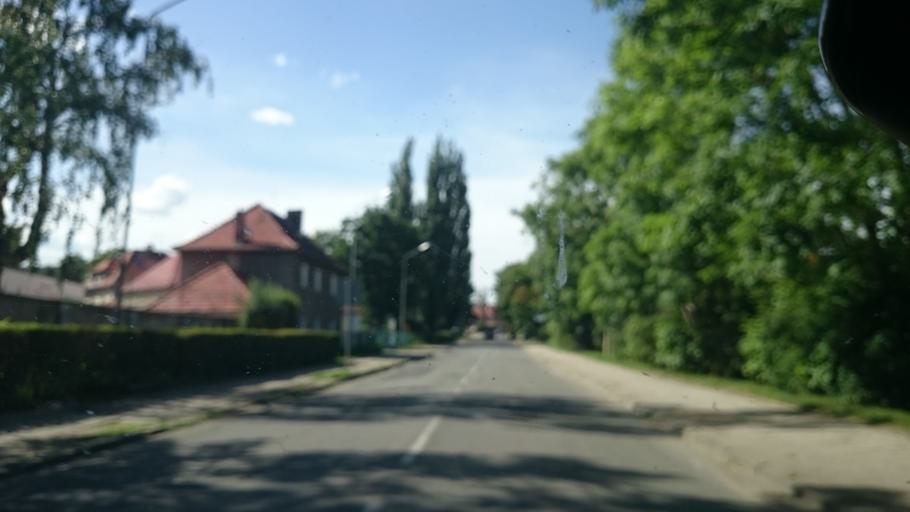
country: PL
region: Lower Silesian Voivodeship
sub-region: Powiat klodzki
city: Polanica-Zdroj
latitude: 50.3985
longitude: 16.5164
